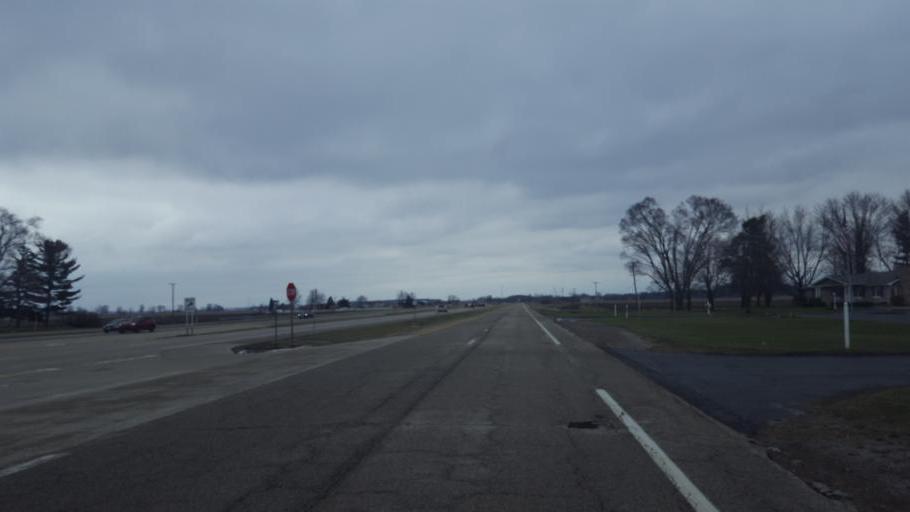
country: US
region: Ohio
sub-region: Delaware County
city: Delaware
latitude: 40.4126
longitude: -83.0739
